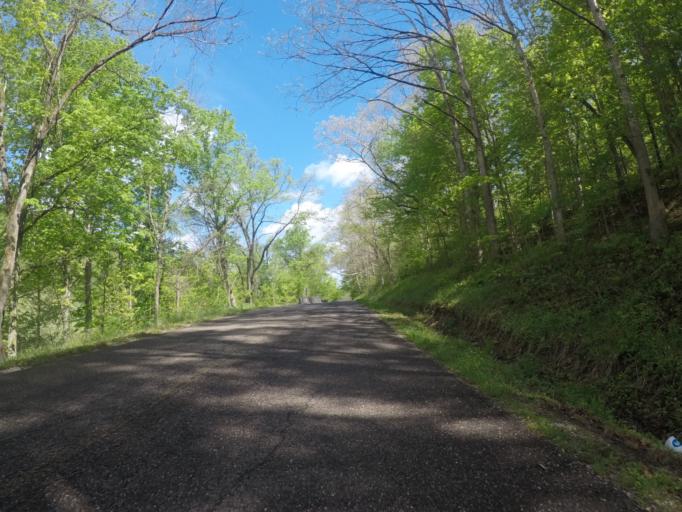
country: US
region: West Virginia
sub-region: Cabell County
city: Huntington
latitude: 38.5148
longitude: -82.4391
